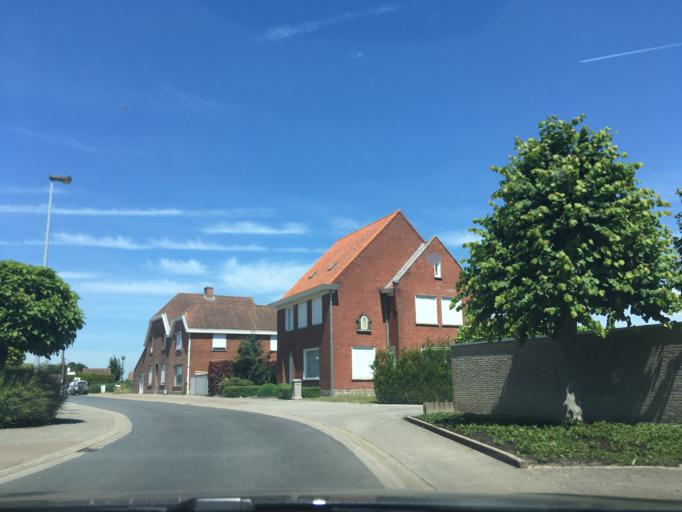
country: BE
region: Flanders
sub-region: Provincie West-Vlaanderen
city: Pittem
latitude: 51.0168
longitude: 3.2582
